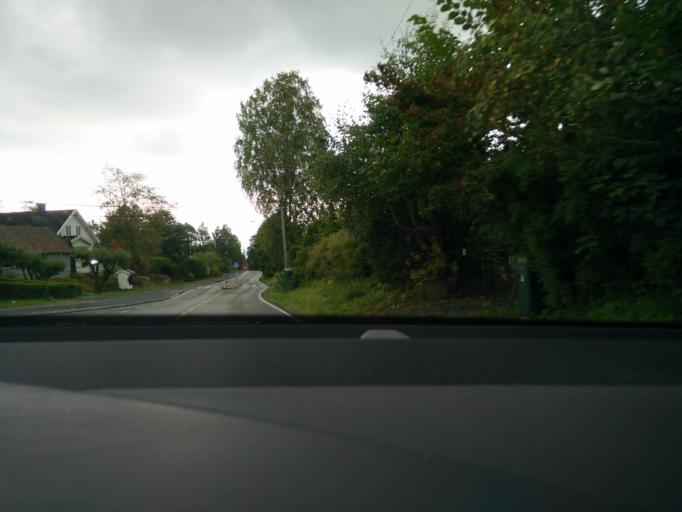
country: NO
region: Akershus
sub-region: Baerum
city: Lysaker
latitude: 59.9324
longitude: 10.6134
